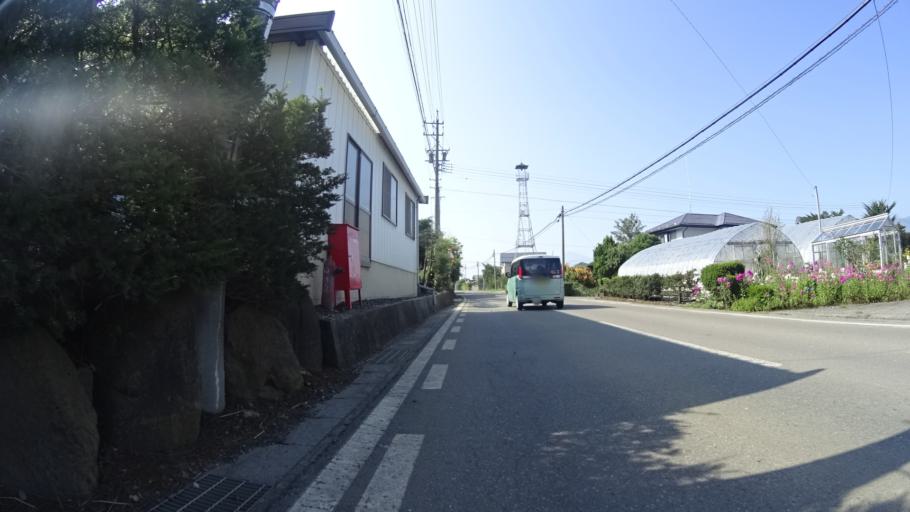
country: JP
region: Nagano
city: Chino
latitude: 35.9519
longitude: 138.2387
